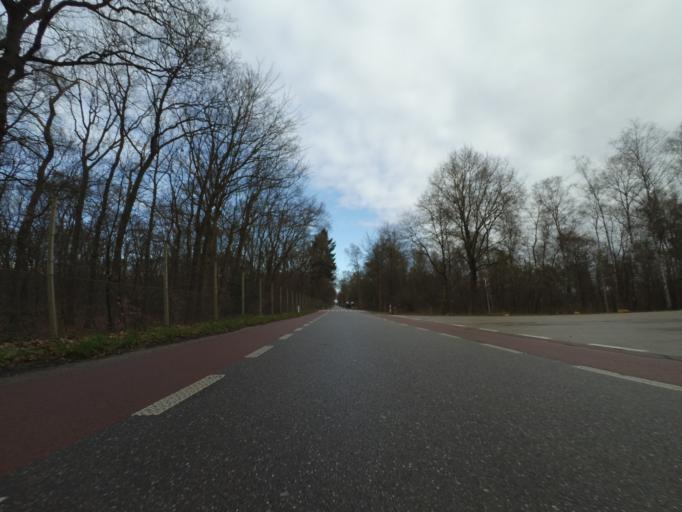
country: NL
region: Gelderland
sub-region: Gemeente Arnhem
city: Gulden Bodem
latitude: 52.0399
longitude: 5.9053
